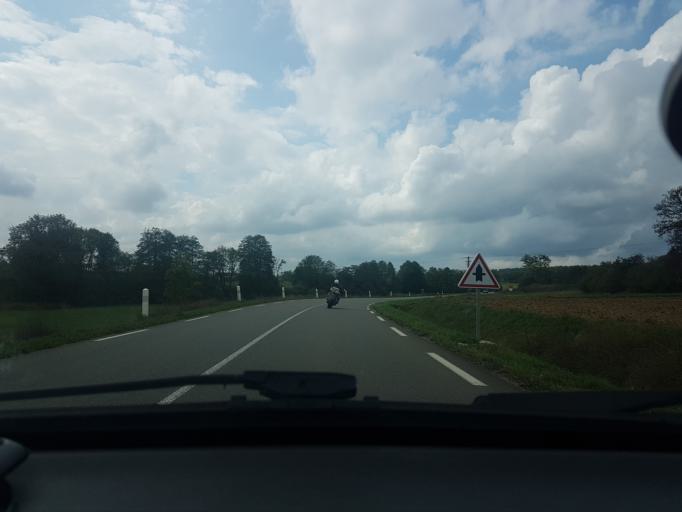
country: FR
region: Franche-Comte
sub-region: Departement du Doubs
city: Arcey
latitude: 47.5637
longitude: 6.6439
